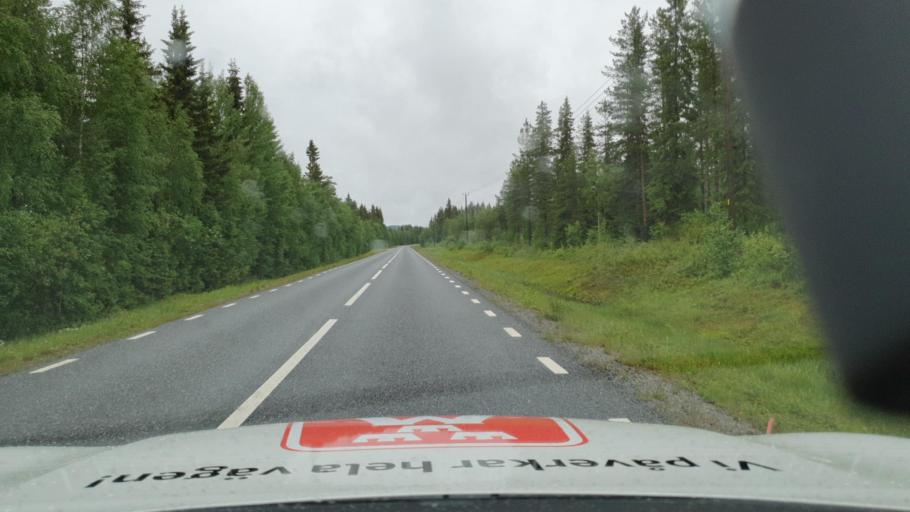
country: SE
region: Vaesterbotten
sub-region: Asele Kommun
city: Asele
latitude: 63.9892
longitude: 17.2646
